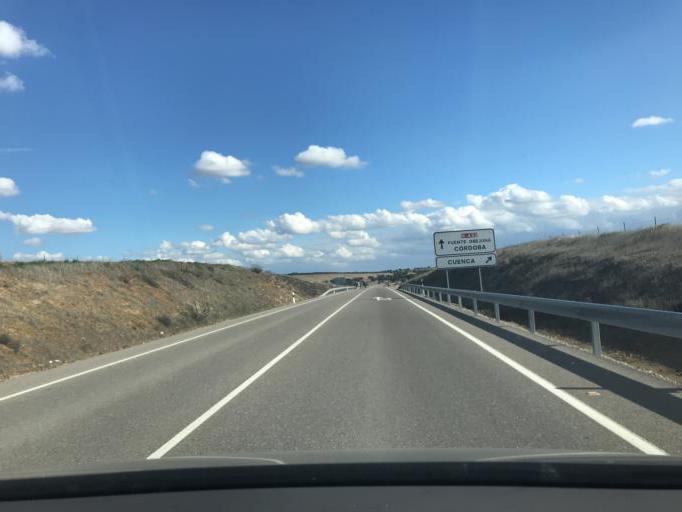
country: ES
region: Extremadura
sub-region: Provincia de Badajoz
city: Granja de Torrehermosa
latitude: 38.2896
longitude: -5.5298
